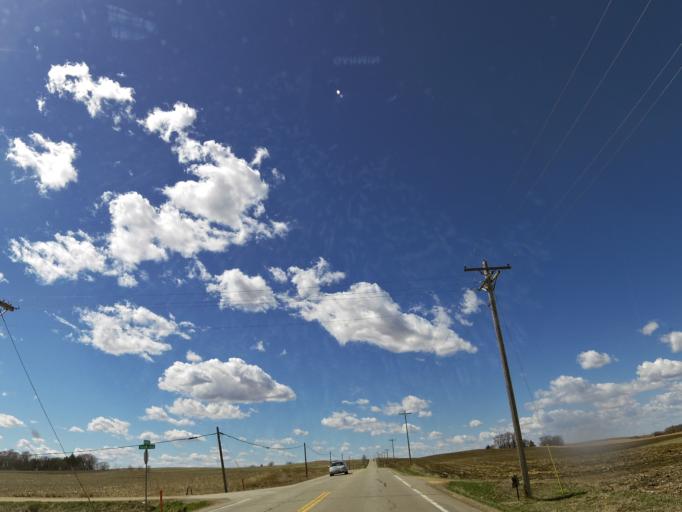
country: US
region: Minnesota
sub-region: Dakota County
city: Hastings
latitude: 44.7566
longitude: -92.9036
